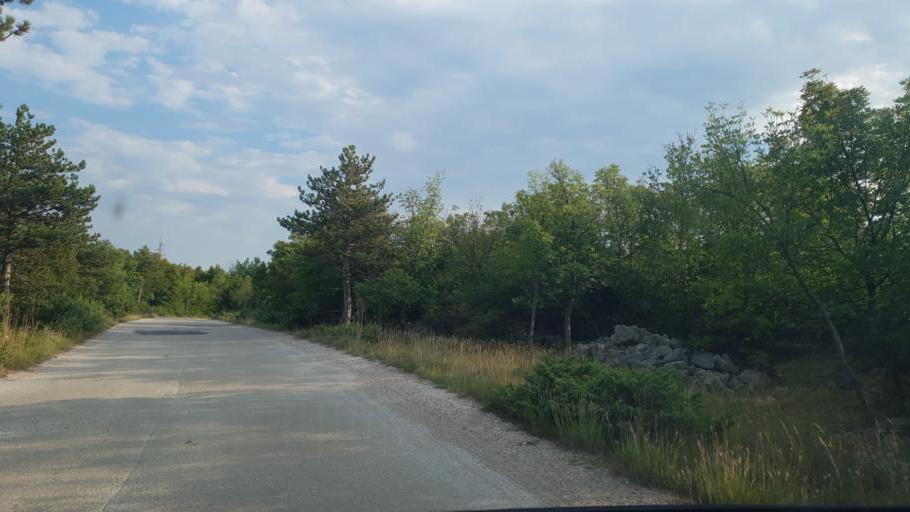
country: HR
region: Primorsko-Goranska
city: Omisalj
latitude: 45.2267
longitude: 14.5724
